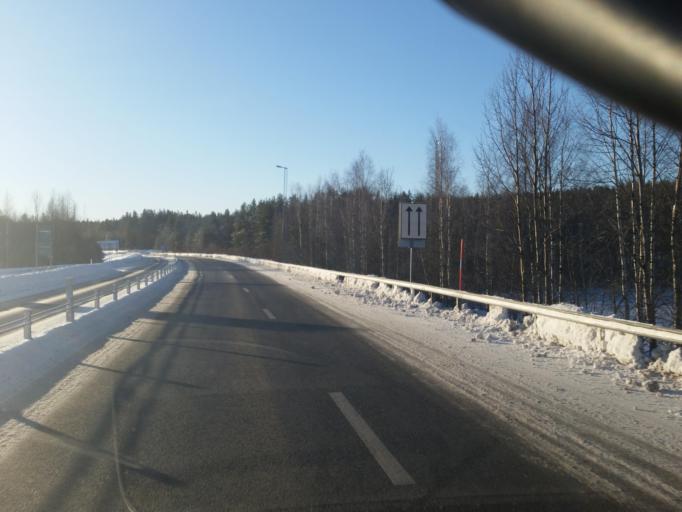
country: SE
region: Norrbotten
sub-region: Pitea Kommun
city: Bergsviken
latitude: 65.3106
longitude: 21.4078
